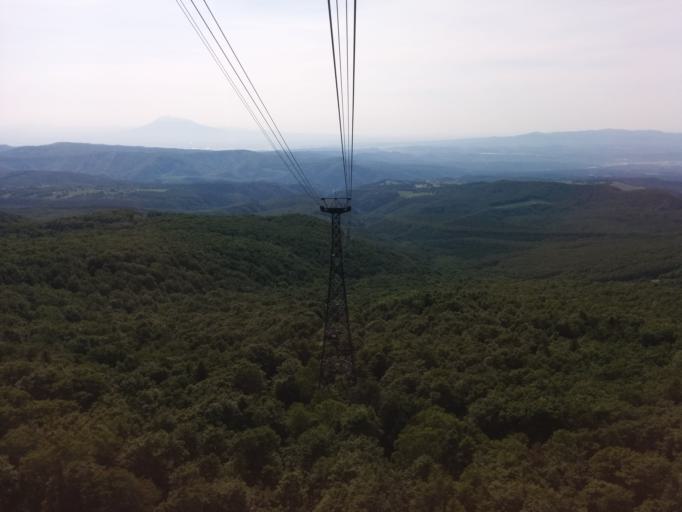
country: JP
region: Aomori
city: Aomori Shi
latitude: 40.6779
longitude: 140.8479
